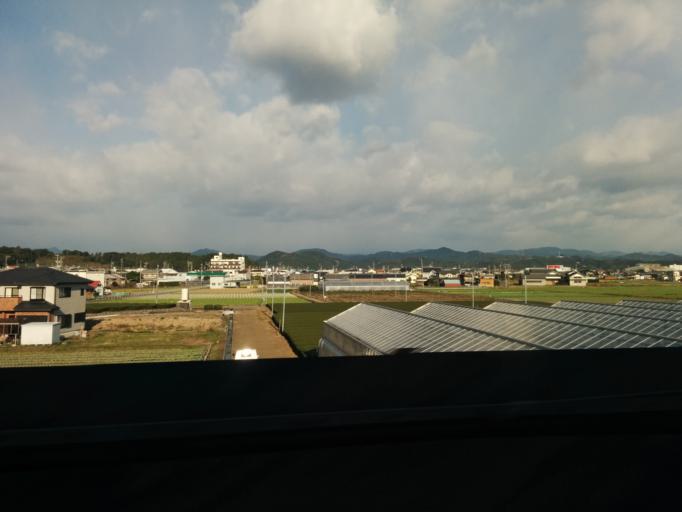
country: JP
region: Shizuoka
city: Shimada
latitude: 34.8117
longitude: 138.2181
